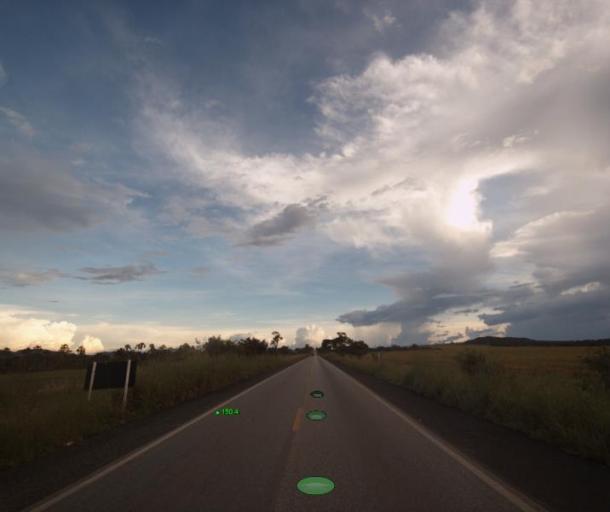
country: BR
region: Goias
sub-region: Uruacu
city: Uruacu
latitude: -14.0894
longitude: -49.1000
